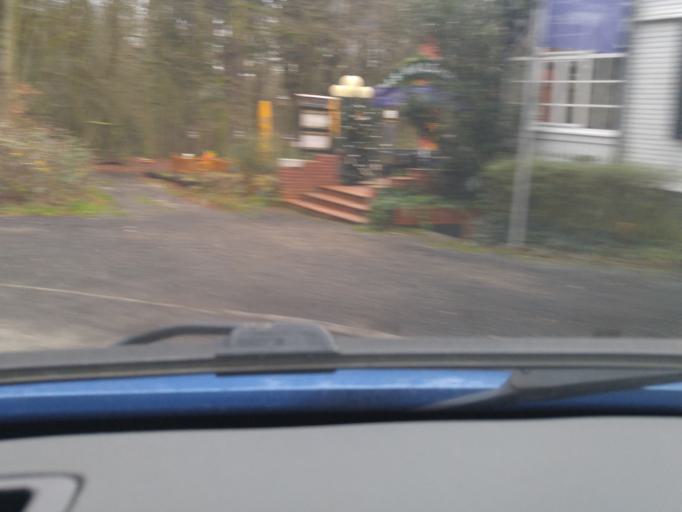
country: DE
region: Hesse
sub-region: Regierungsbezirk Darmstadt
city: Bad Nauheim
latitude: 50.3559
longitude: 8.7203
